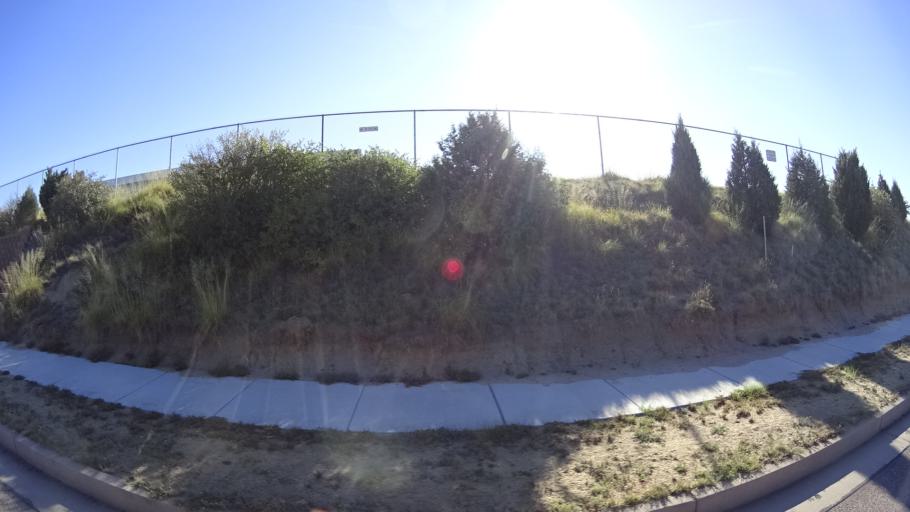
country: US
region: Colorado
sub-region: El Paso County
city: Security-Widefield
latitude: 38.8045
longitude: -104.7236
